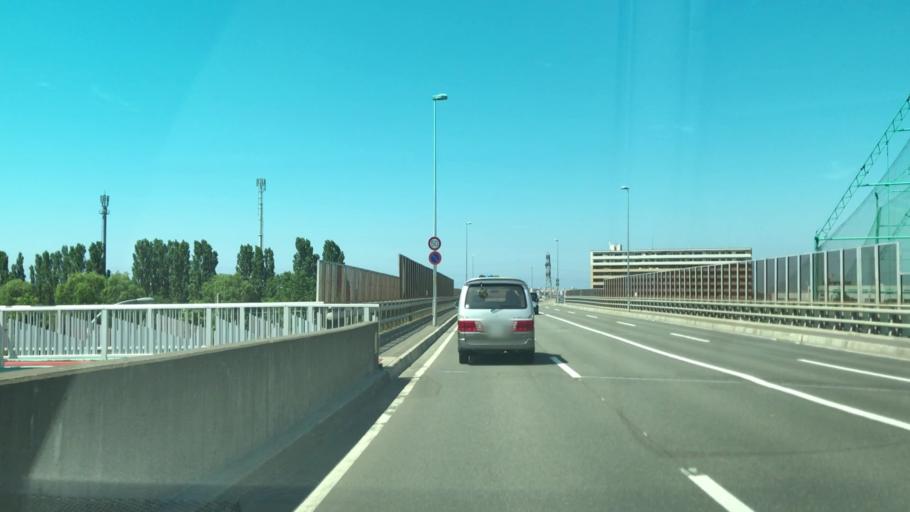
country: JP
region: Hokkaido
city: Sapporo
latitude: 43.1235
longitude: 141.2359
